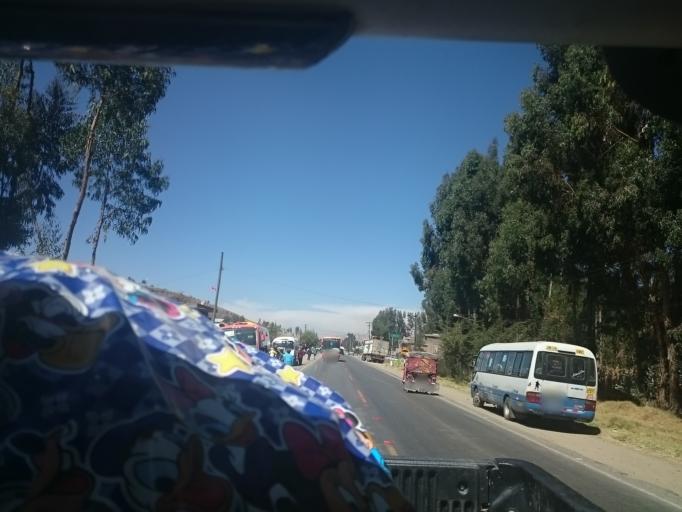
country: PE
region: Junin
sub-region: Provincia de Jauja
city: San Lorenzo
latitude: -11.8648
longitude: -75.3733
